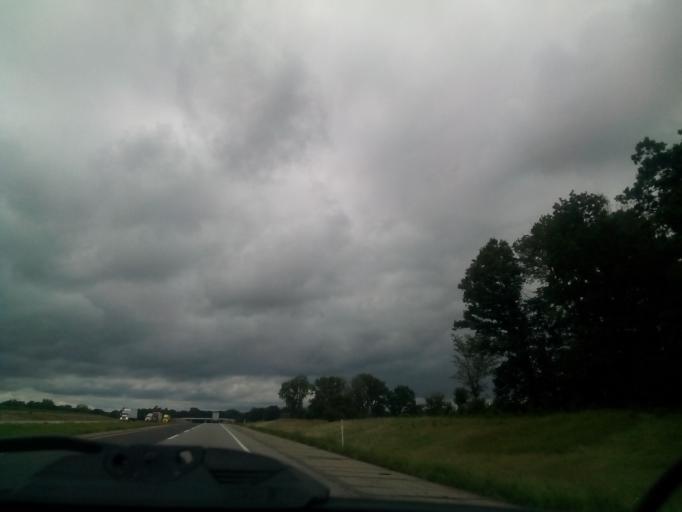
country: US
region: Michigan
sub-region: Branch County
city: Bronson
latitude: 41.7435
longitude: -85.2754
